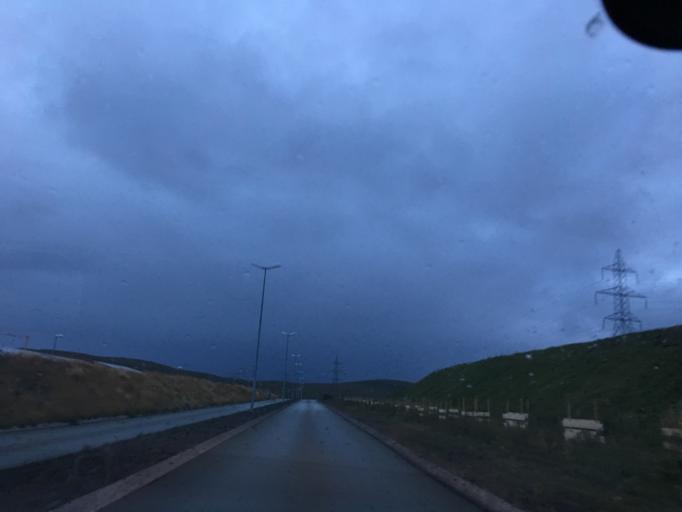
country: IS
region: Capital Region
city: Hafnarfjoerdur
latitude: 64.0412
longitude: -21.9733
